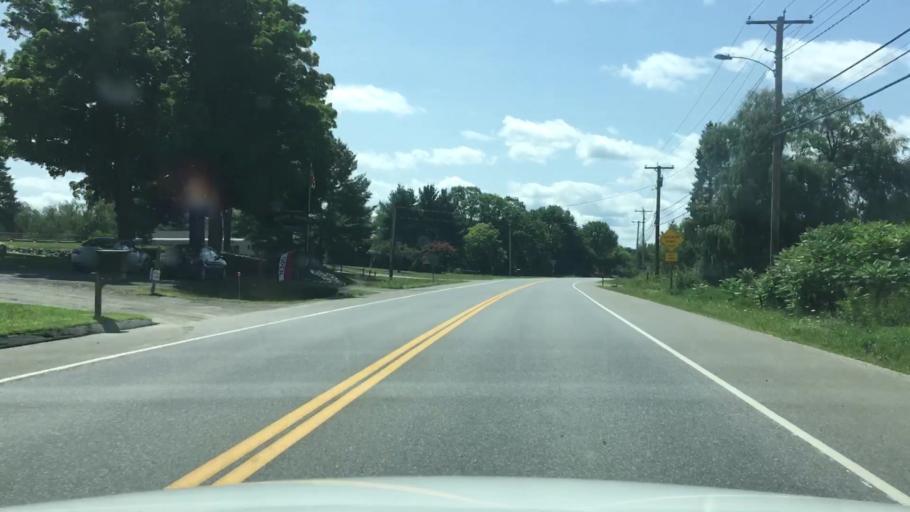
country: US
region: Maine
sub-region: Kennebec County
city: Augusta
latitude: 44.2949
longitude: -69.7684
